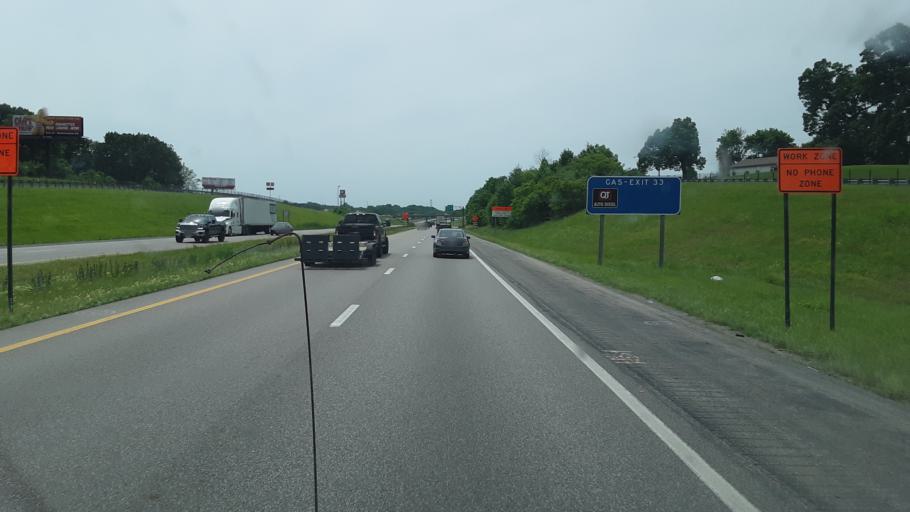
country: US
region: Missouri
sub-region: Saint Louis County
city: Glasgow Village
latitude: 38.7676
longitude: -90.1956
